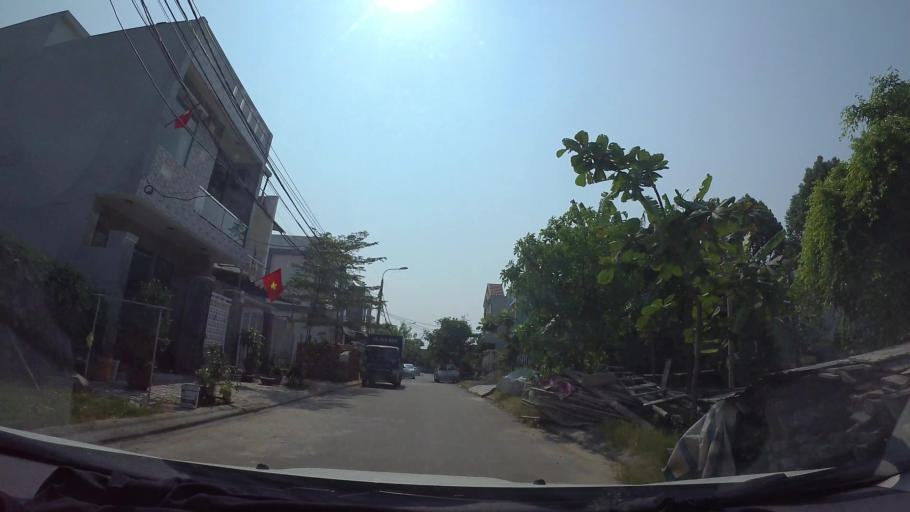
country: VN
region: Da Nang
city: Cam Le
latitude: 16.0129
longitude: 108.1983
